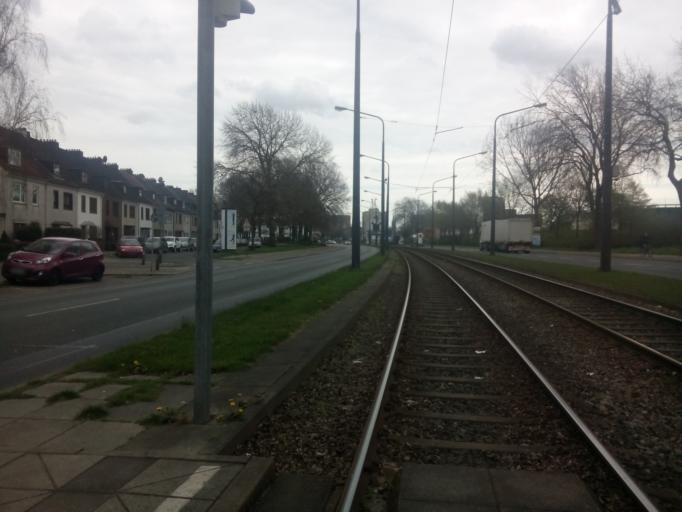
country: DE
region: Bremen
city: Bremen
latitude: 53.0911
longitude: 8.7821
